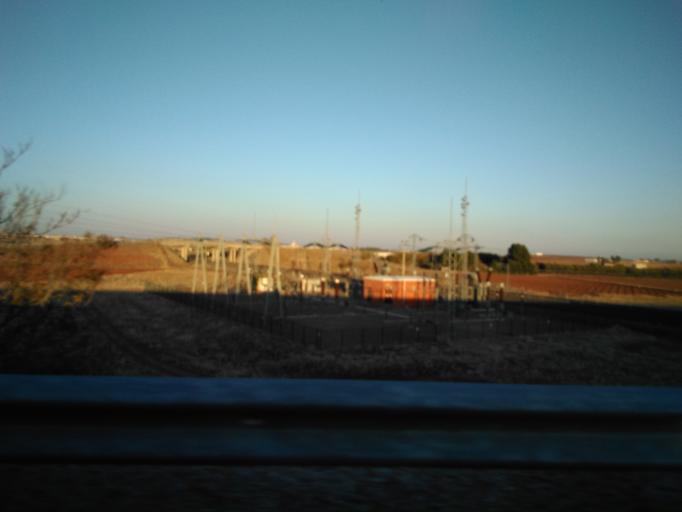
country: ES
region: Castille-La Mancha
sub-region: Provincia de Ciudad Real
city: Miguelturra
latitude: 38.9569
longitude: -3.9200
